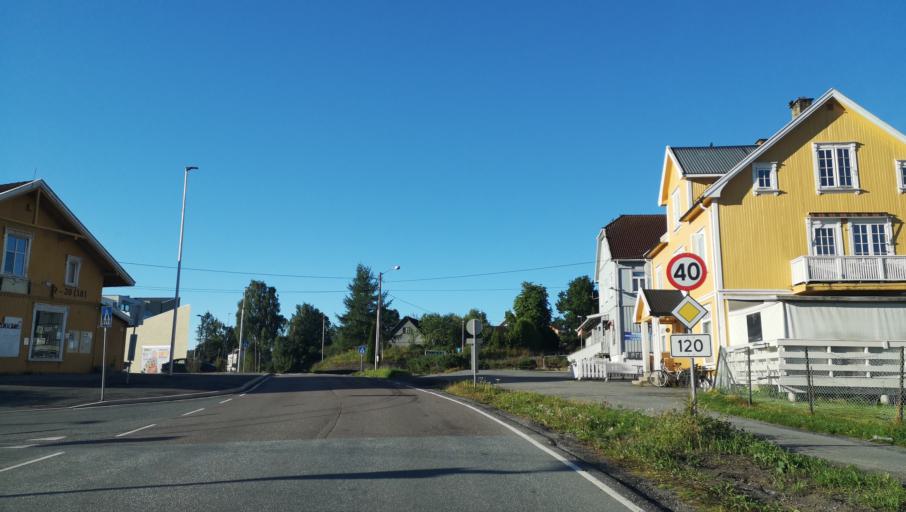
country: NO
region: Ostfold
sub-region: Hobol
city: Tomter
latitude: 59.6604
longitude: 11.0001
